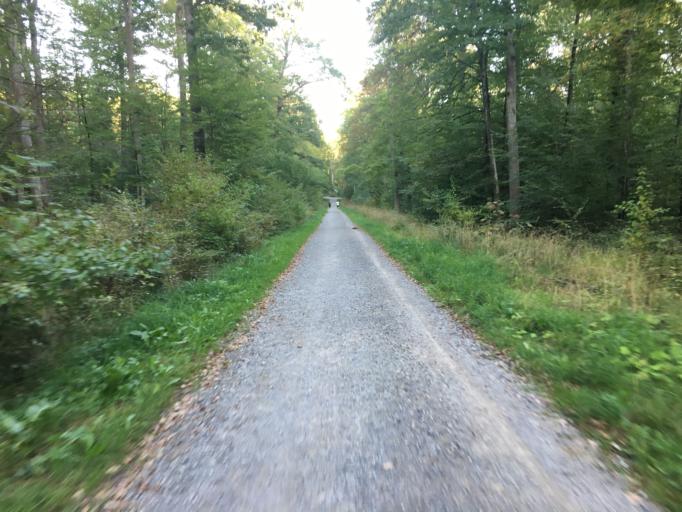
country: DE
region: Baden-Wuerttemberg
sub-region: Regierungsbezirk Stuttgart
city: Boeblingen
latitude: 48.6657
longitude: 8.9941
